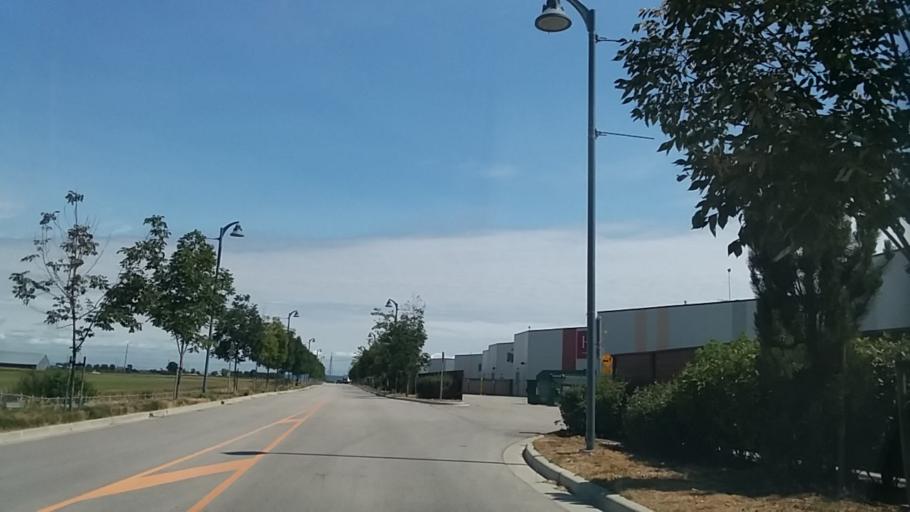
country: CA
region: British Columbia
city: Ladner
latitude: 49.0431
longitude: -123.0869
